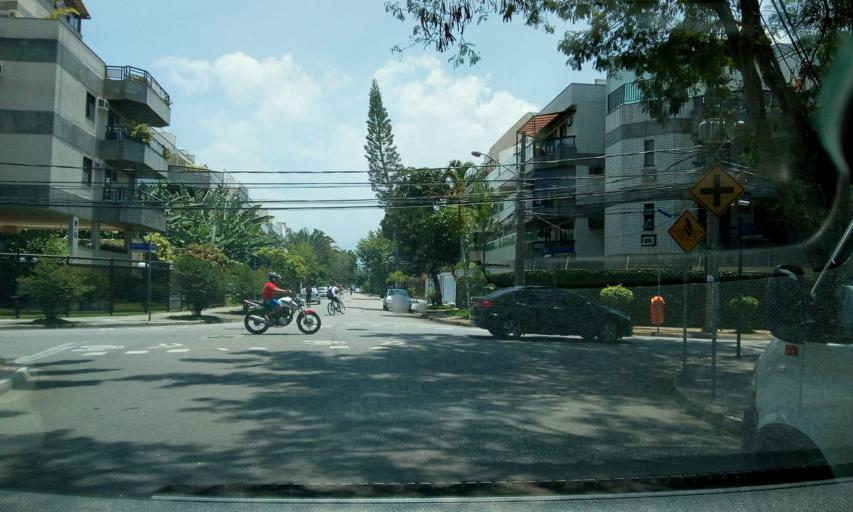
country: BR
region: Rio de Janeiro
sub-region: Nilopolis
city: Nilopolis
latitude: -23.0217
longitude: -43.4609
